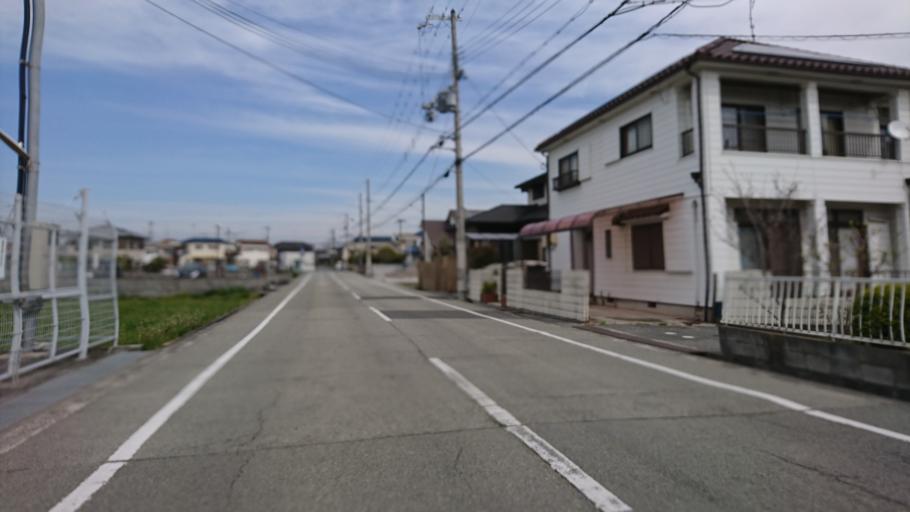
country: JP
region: Hyogo
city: Kakogawacho-honmachi
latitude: 34.7261
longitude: 134.8815
